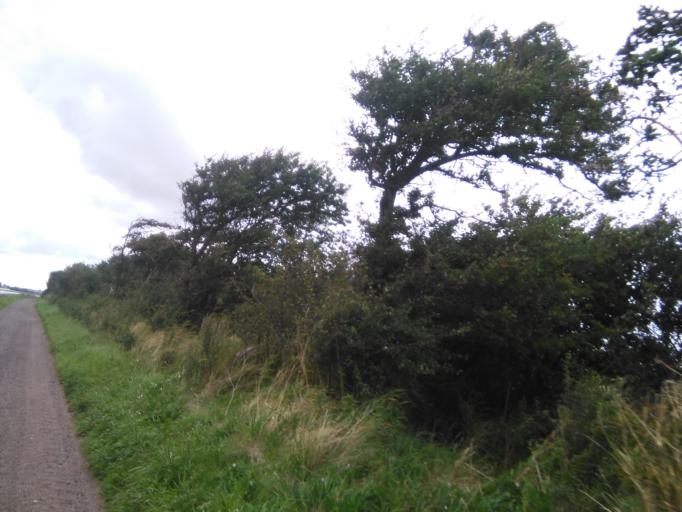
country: DK
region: Central Jutland
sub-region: Odder Kommune
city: Odder
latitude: 55.8645
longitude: 10.1404
